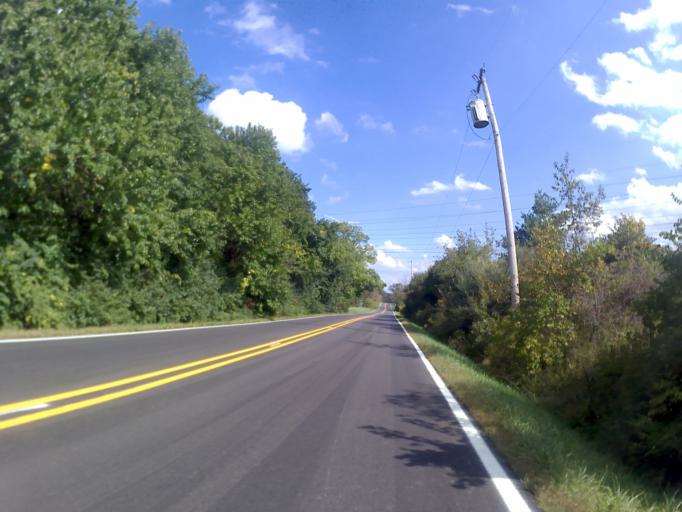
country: US
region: Illinois
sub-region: DuPage County
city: Woodridge
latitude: 41.7421
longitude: -88.0858
